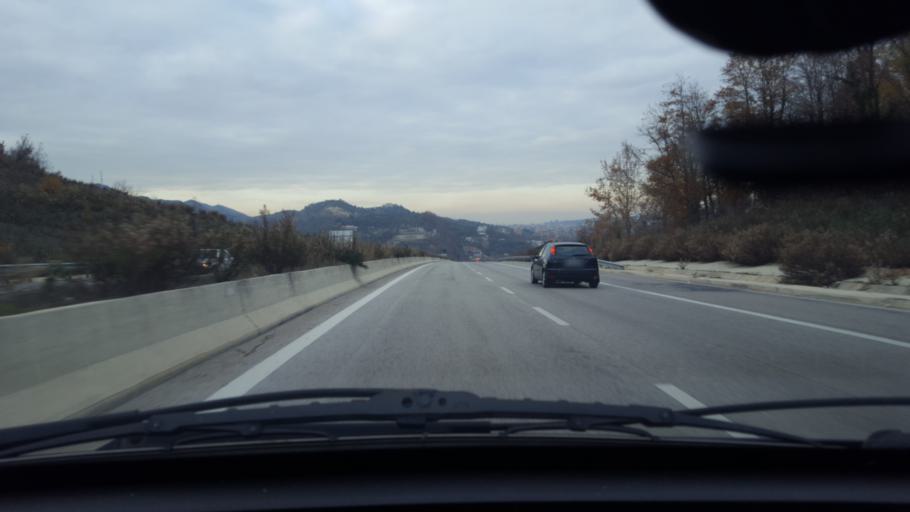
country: AL
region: Tirane
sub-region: Rrethi i Tiranes
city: Petrele
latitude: 41.2700
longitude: 19.8619
